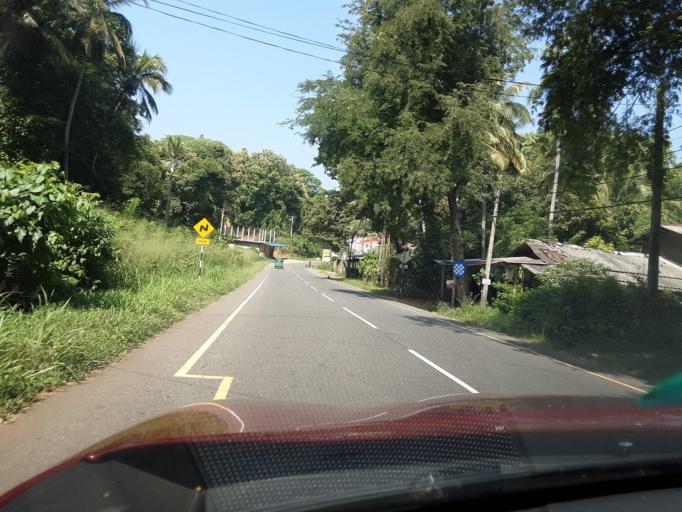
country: LK
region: Uva
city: Badulla
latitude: 7.1941
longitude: 81.0263
